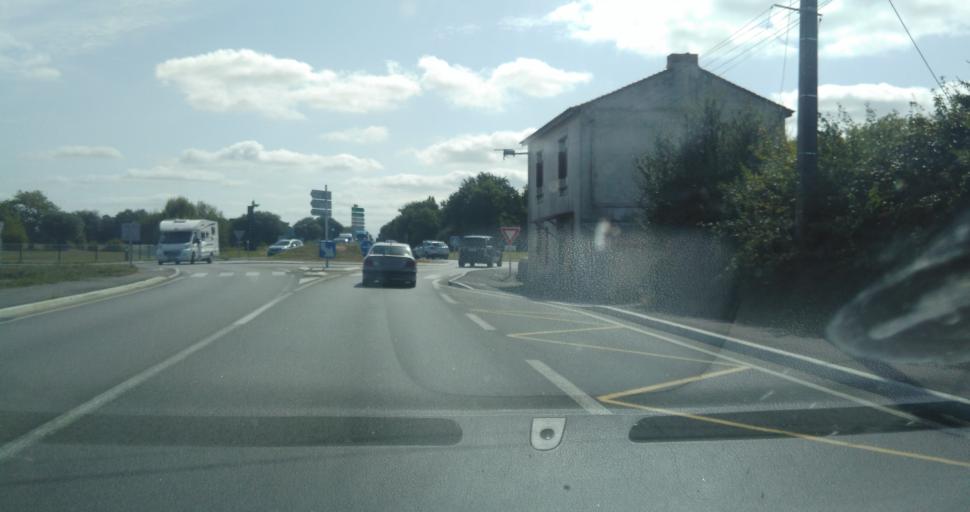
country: FR
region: Pays de la Loire
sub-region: Departement de la Vendee
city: Chateau-d'Olonne
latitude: 46.4788
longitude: -1.6886
